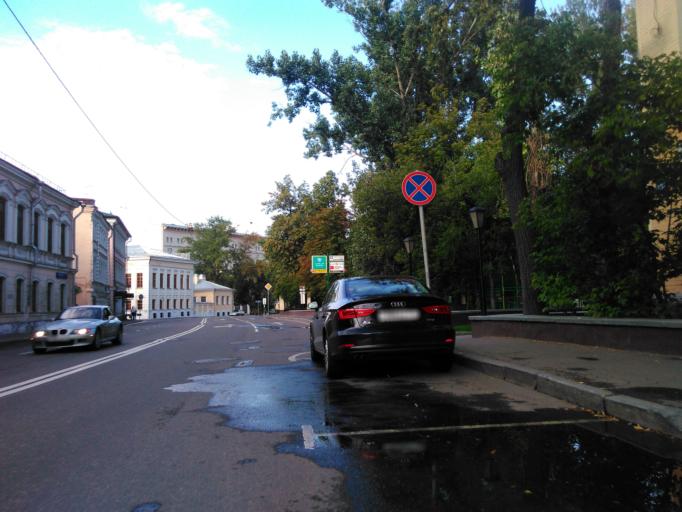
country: RU
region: Moscow
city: Taganskiy
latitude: 55.7538
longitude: 37.6534
